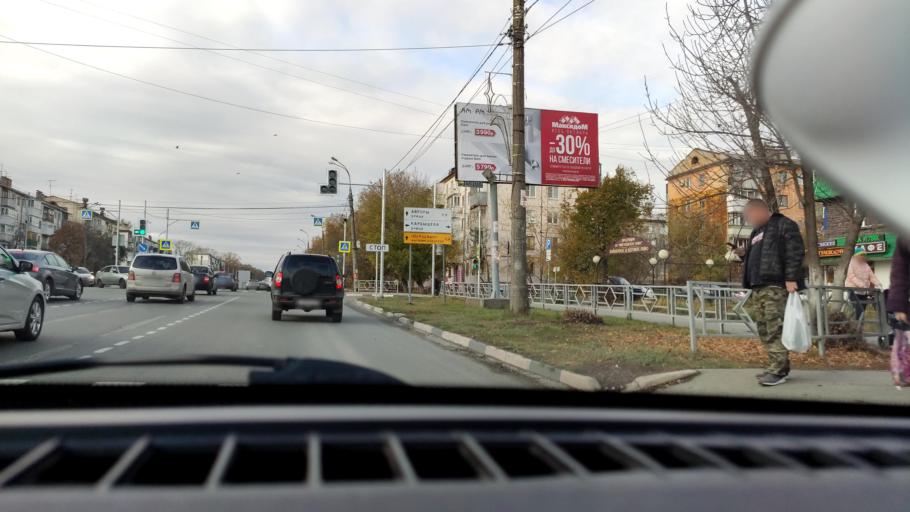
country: RU
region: Samara
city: Samara
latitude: 53.2012
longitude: 50.2043
